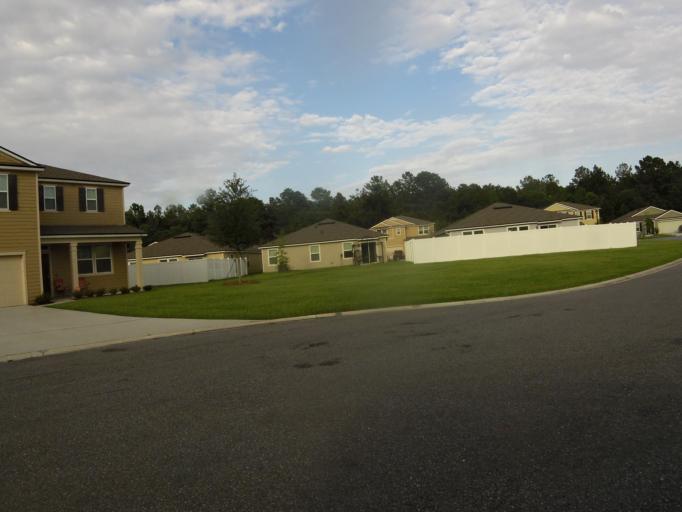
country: US
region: Florida
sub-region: Duval County
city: Jacksonville
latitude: 30.3598
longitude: -81.7704
